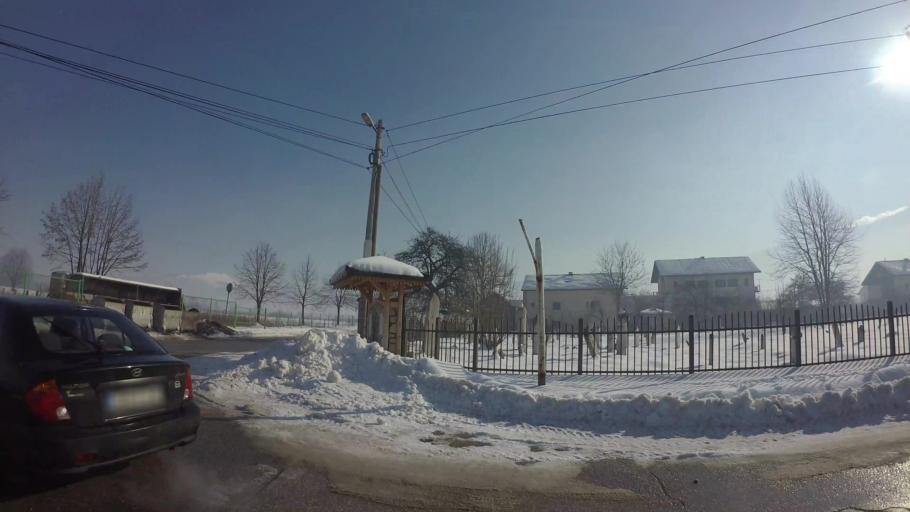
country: BA
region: Federation of Bosnia and Herzegovina
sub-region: Kanton Sarajevo
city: Sarajevo
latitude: 43.8041
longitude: 18.3037
